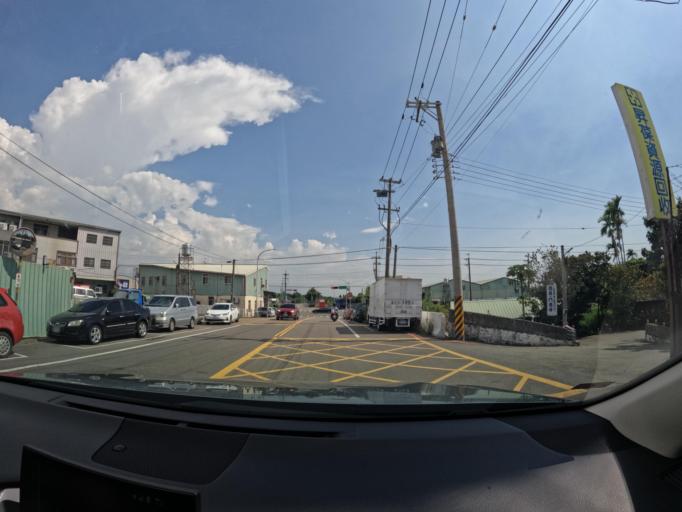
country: TW
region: Taiwan
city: Fengyuan
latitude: 24.3032
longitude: 120.7176
